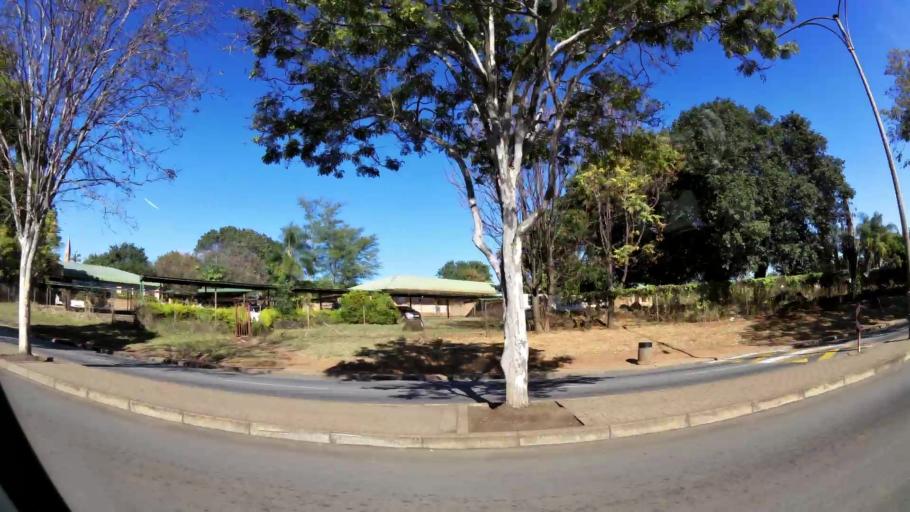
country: ZA
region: Limpopo
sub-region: Mopani District Municipality
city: Tzaneen
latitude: -23.8308
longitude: 30.1641
